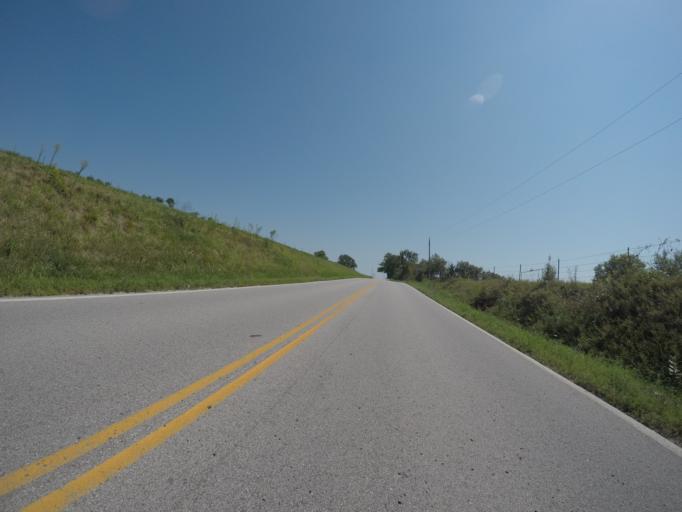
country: US
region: Kansas
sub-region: Leavenworth County
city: Lansing
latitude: 39.2354
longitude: -94.8646
